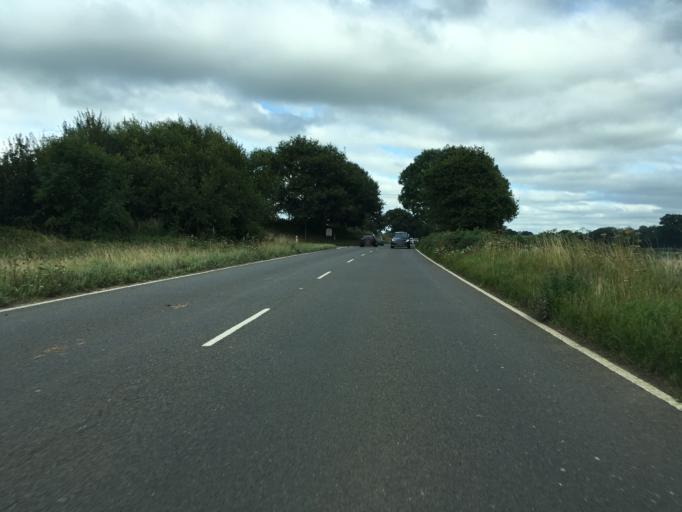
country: GB
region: England
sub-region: Hampshire
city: Liss
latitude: 51.0067
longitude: -0.8709
